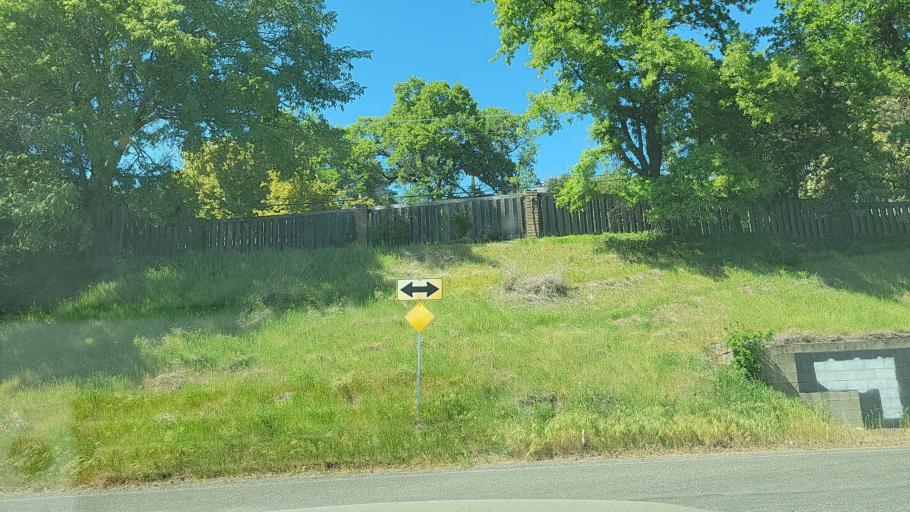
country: US
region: California
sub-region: Tehama County
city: Red Bluff
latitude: 40.1959
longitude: -122.2268
